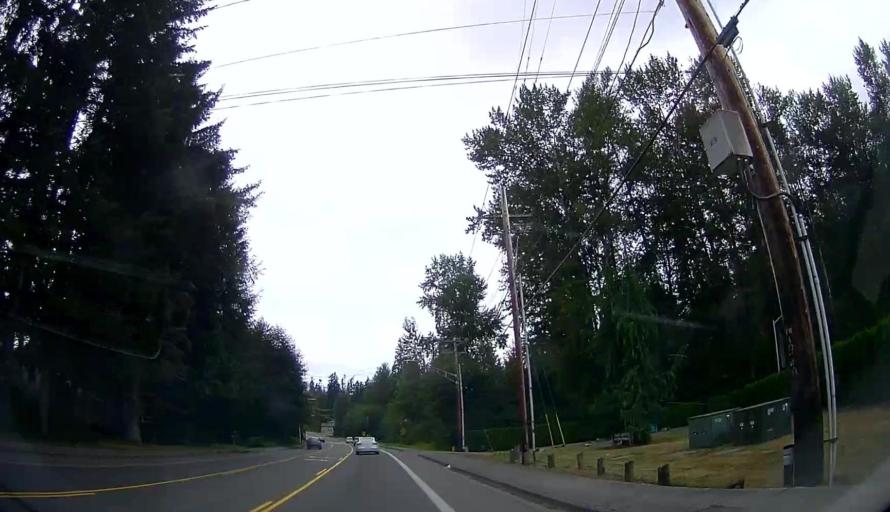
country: US
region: Washington
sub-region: Snohomish County
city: Marysville
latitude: 48.0521
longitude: -122.2093
